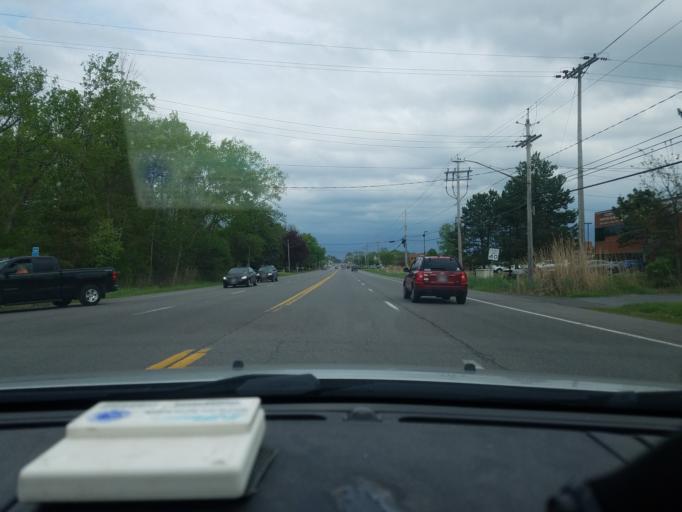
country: US
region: New York
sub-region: Onondaga County
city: Galeville
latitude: 43.1216
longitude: -76.1671
